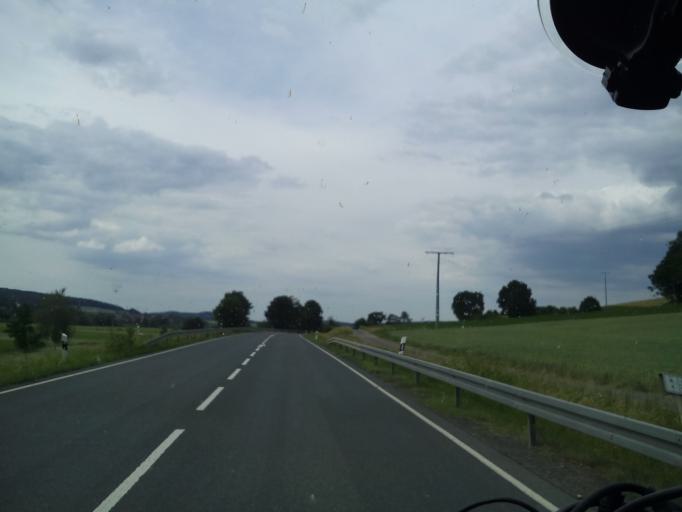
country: DE
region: Bavaria
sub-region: Regierungsbezirk Unterfranken
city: Untermerzbach
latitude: 50.1106
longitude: 10.8691
